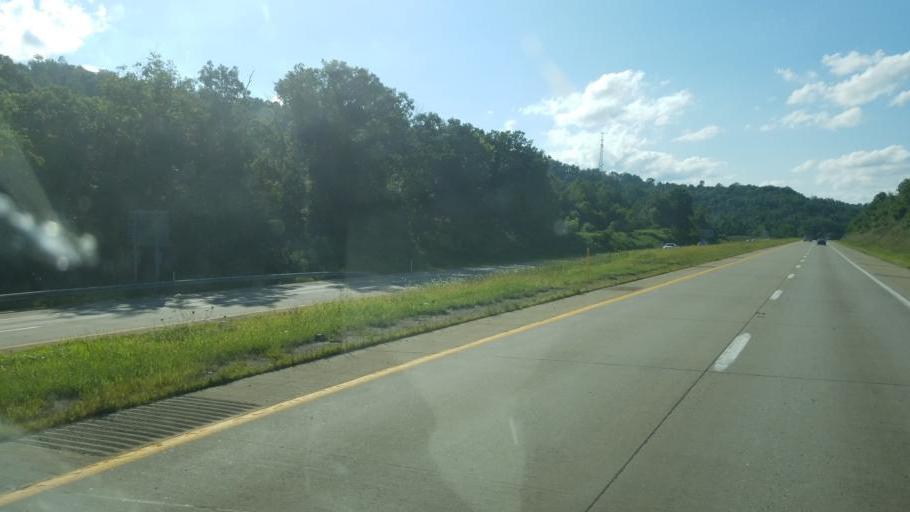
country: US
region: Pennsylvania
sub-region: Greene County
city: Morrisville
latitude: 39.9088
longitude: -80.1532
